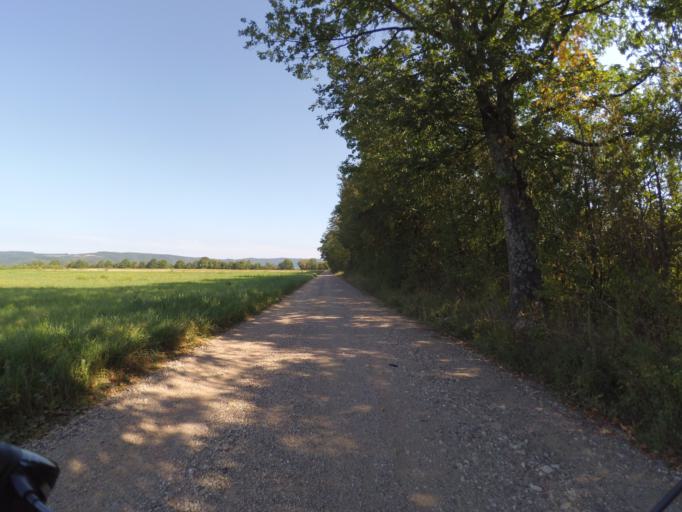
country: DE
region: Rheinland-Pfalz
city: Trittenheim
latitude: 49.8471
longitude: 6.9095
